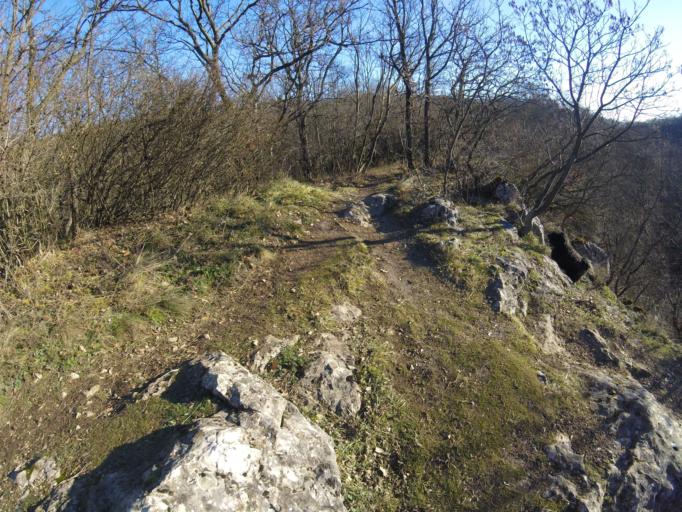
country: HU
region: Pest
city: Pilisszentkereszt
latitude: 47.6854
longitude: 18.9150
